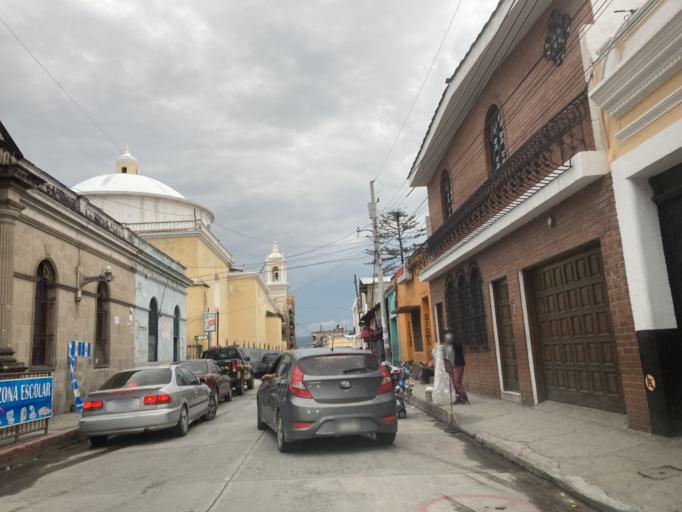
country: GT
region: Huehuetenango
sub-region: Municipio de Huehuetenango
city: Huehuetenango
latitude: 15.3213
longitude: -91.4692
